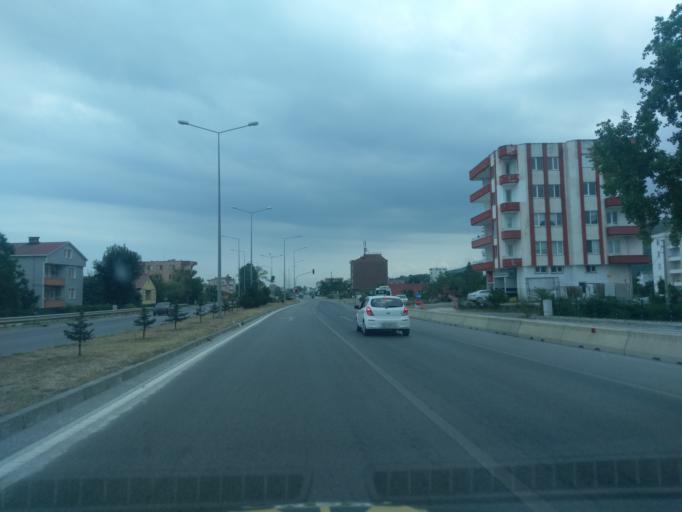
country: TR
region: Samsun
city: Taflan
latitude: 41.4046
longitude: 36.1843
